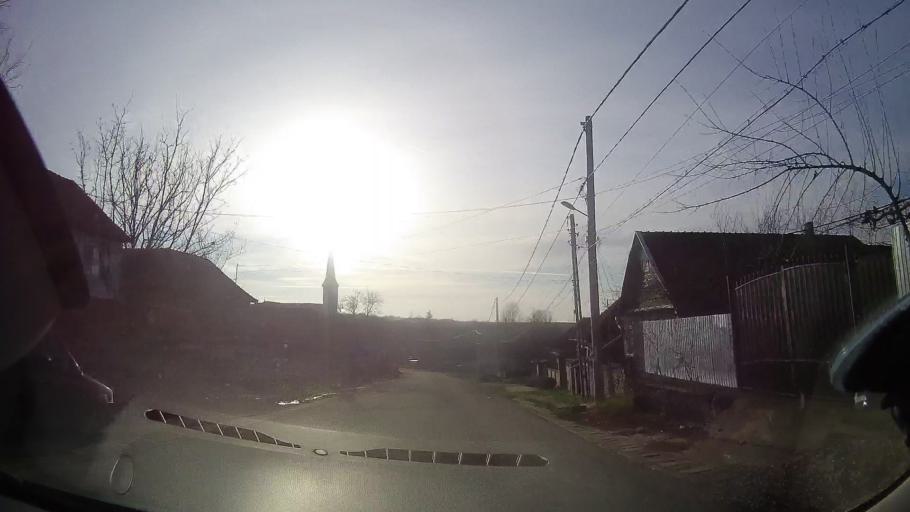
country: RO
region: Bihor
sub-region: Comuna Sarbi
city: Burzuc
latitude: 47.1090
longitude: 22.1718
